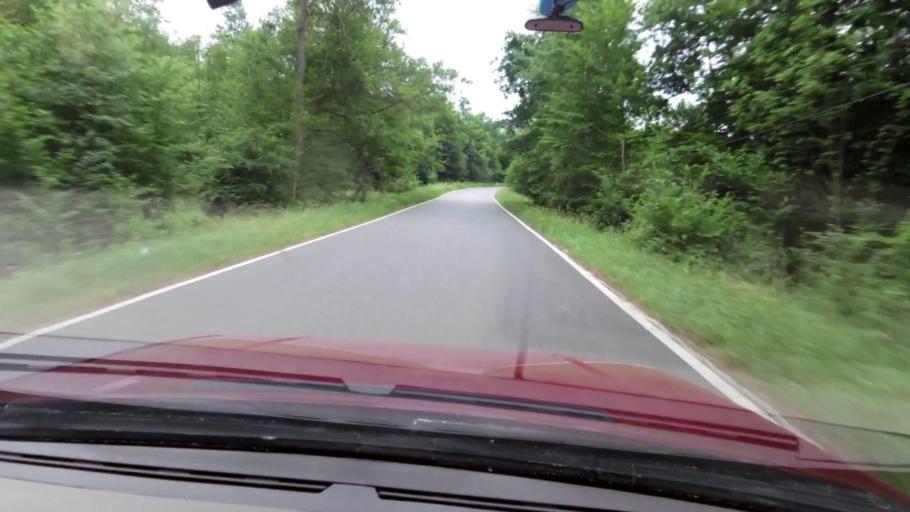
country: PL
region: West Pomeranian Voivodeship
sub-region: Powiat koszalinski
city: Polanow
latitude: 54.1534
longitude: 16.6986
